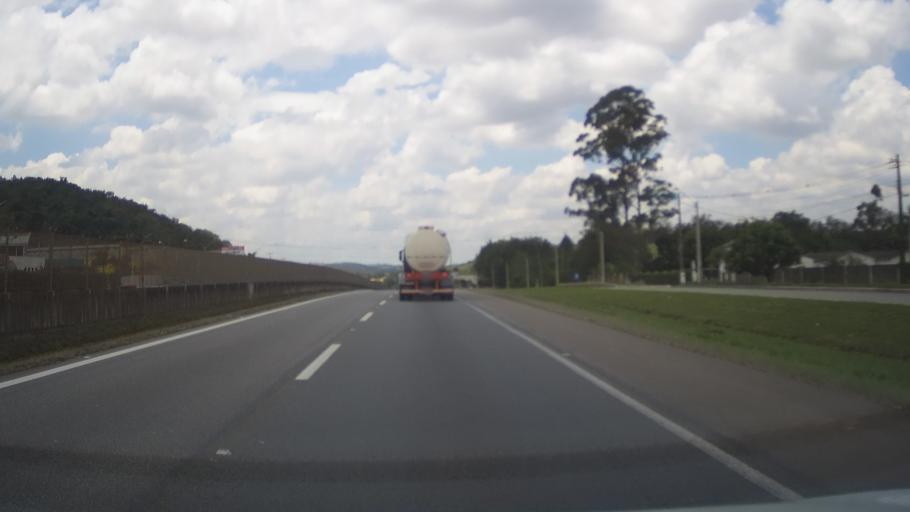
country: BR
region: Minas Gerais
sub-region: Tres Coracoes
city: Tres Coracoes
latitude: -21.6675
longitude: -45.3180
